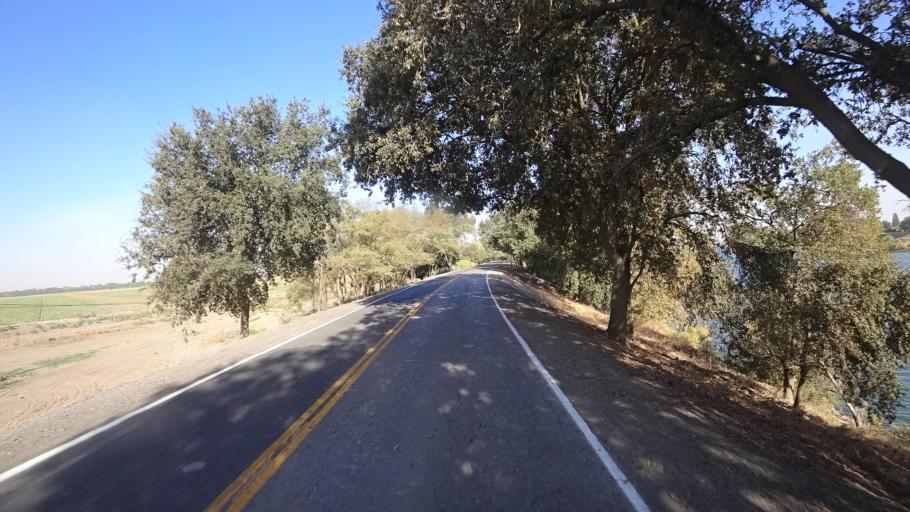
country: US
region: California
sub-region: Yolo County
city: West Sacramento
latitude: 38.4948
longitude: -121.5588
